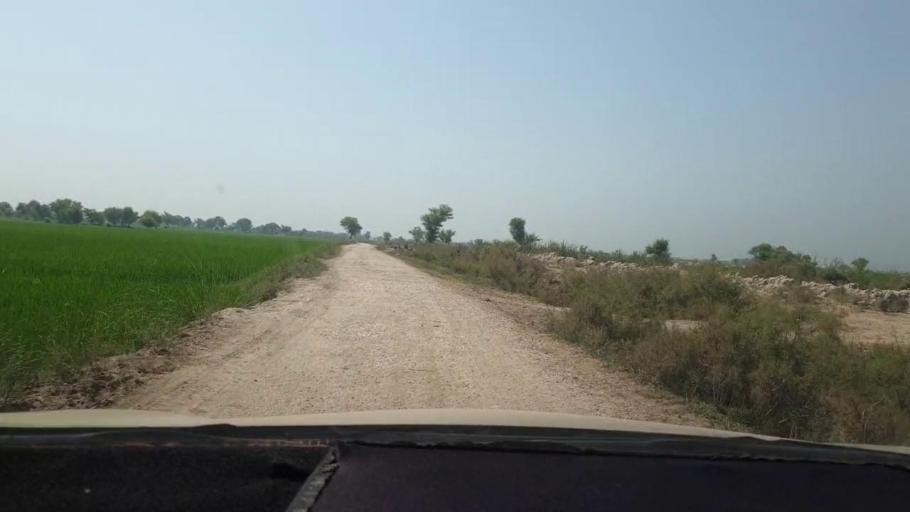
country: PK
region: Sindh
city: Miro Khan
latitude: 27.7131
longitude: 68.0380
